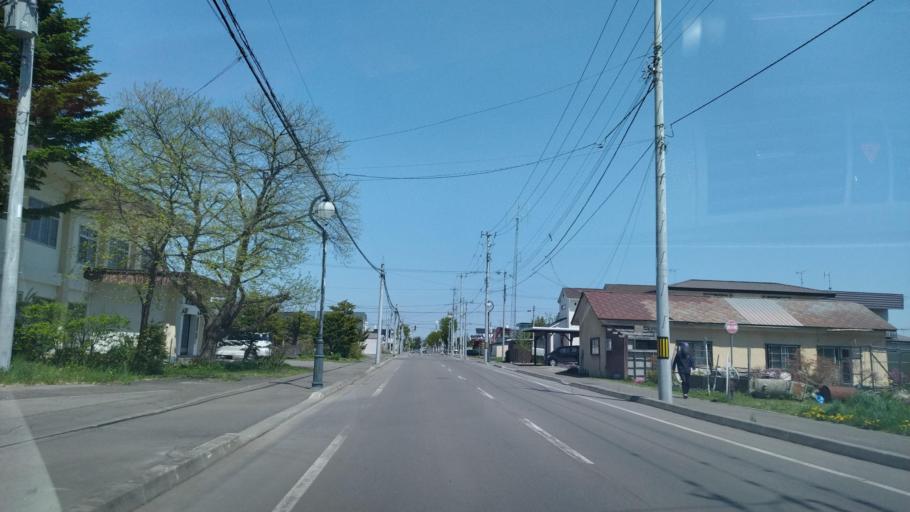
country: JP
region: Hokkaido
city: Otofuke
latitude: 43.2284
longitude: 143.2912
